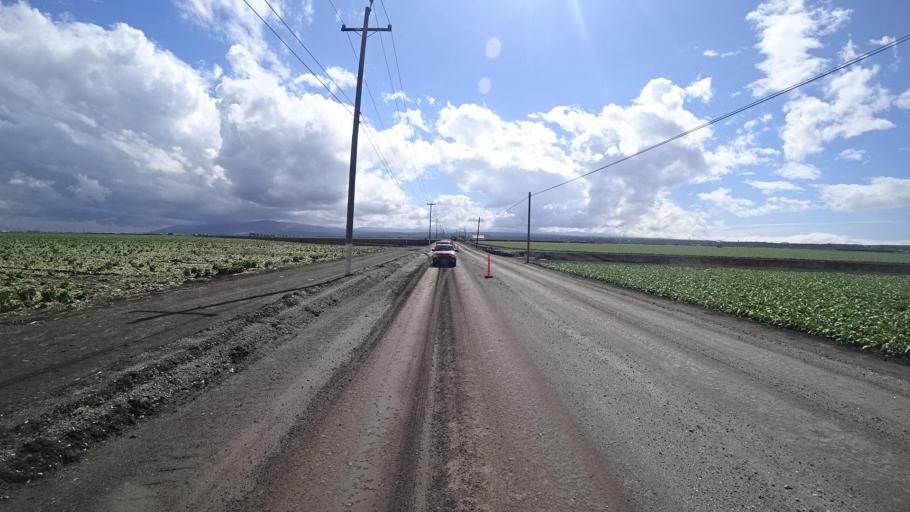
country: US
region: California
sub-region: Monterey County
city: Boronda
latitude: 36.7010
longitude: -121.7309
